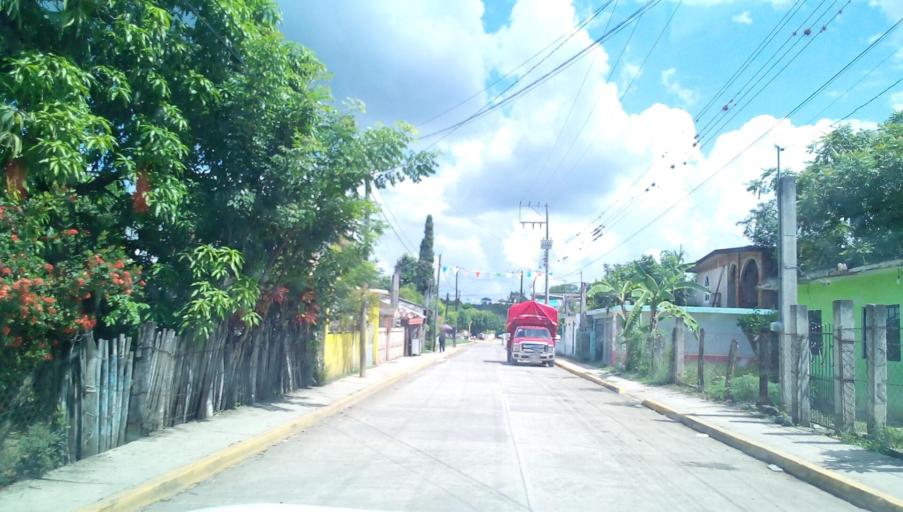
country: MX
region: Veracruz
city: Tamalin
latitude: 21.3589
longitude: -97.7949
